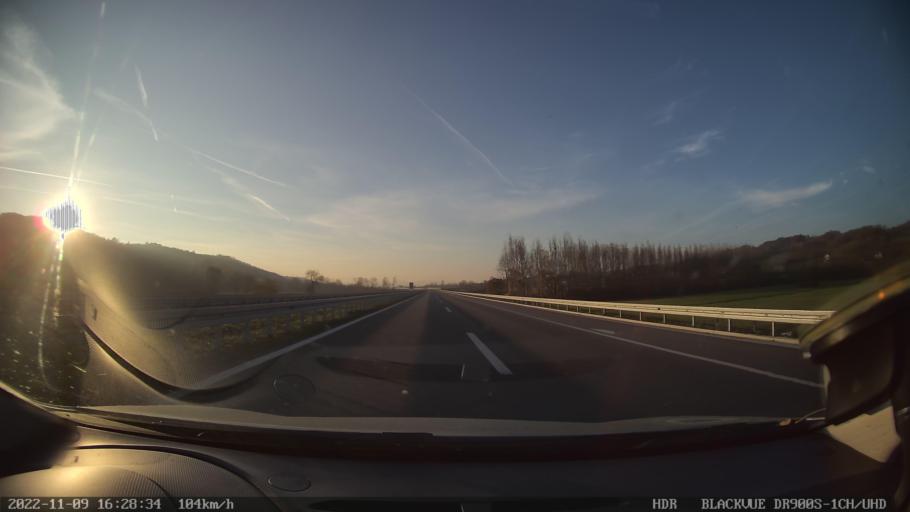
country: RS
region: Central Serbia
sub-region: Moravicki Okrug
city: Cacak
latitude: 43.9210
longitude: 20.3819
